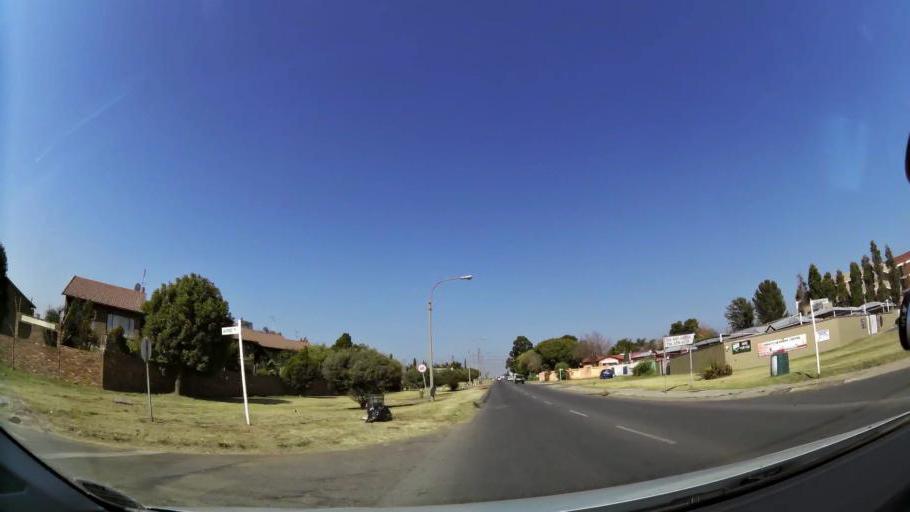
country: ZA
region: Gauteng
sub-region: City of Johannesburg Metropolitan Municipality
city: Modderfontein
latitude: -26.1169
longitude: 28.1695
